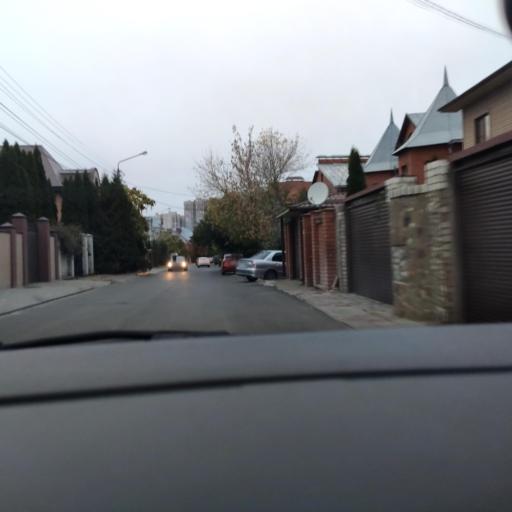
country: RU
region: Voronezj
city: Voronezh
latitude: 51.7061
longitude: 39.2034
